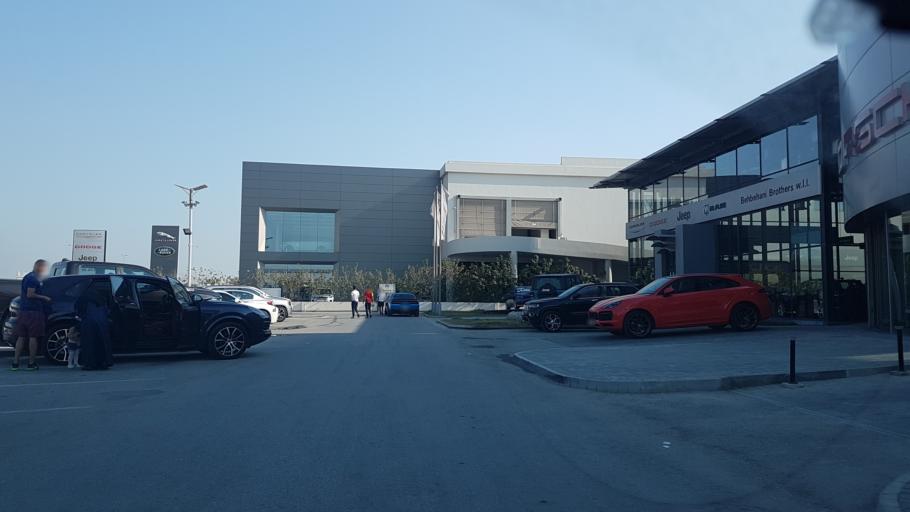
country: BH
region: Northern
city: Sitrah
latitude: 26.1551
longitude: 50.6095
